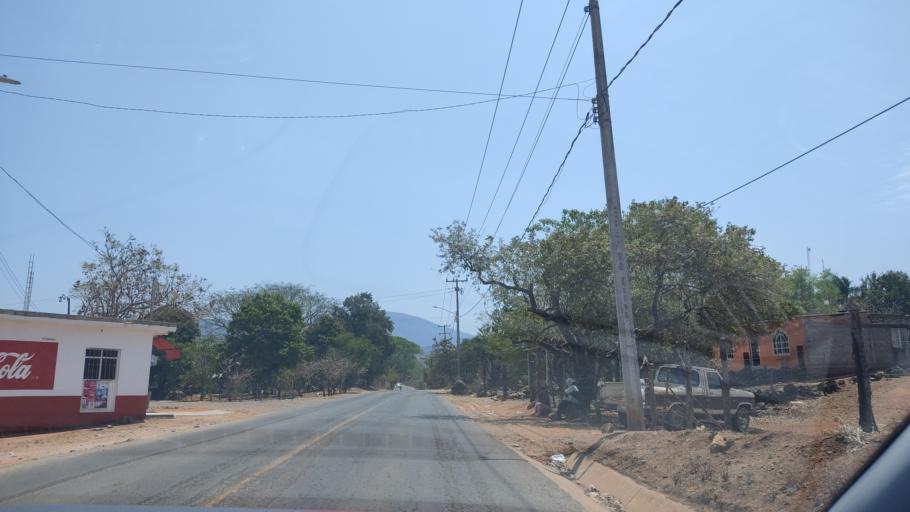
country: MX
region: Nayarit
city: Puga
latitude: 21.5789
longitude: -104.7884
